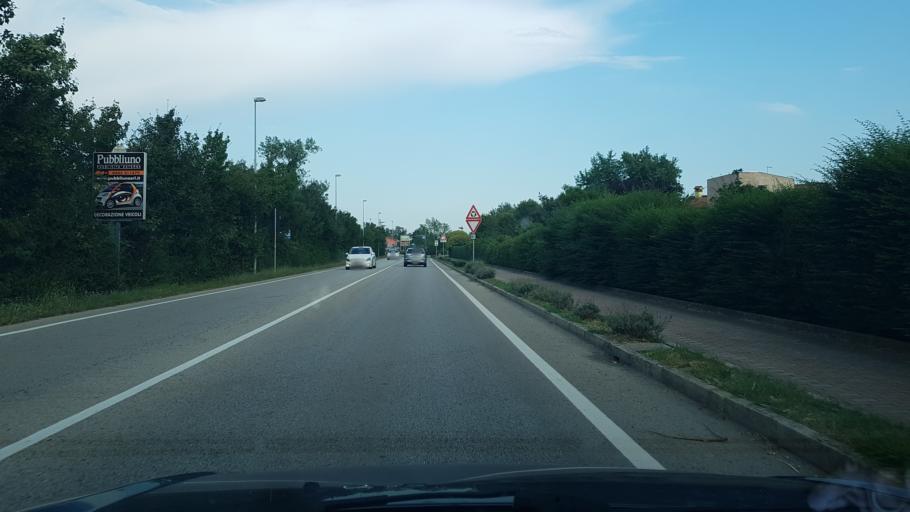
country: IT
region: Veneto
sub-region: Provincia di Vicenza
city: Marano Vicentino
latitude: 45.6987
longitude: 11.4382
